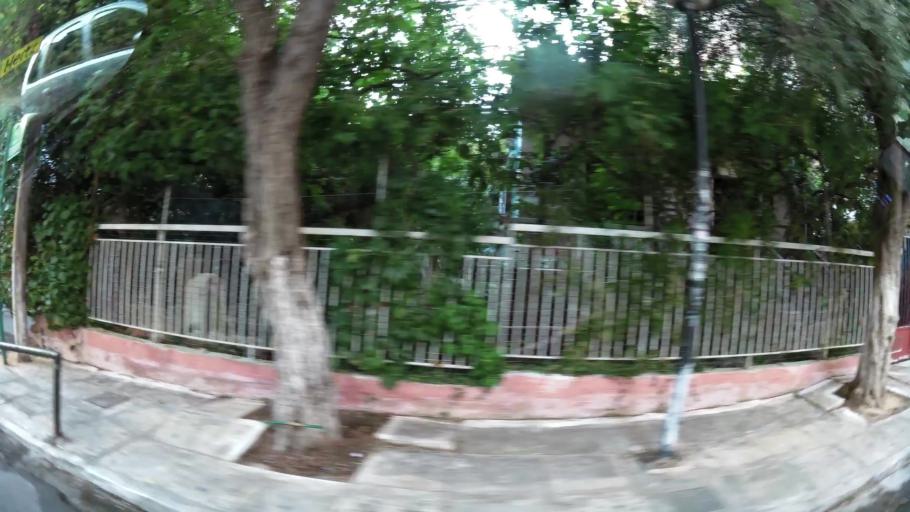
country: GR
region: Attica
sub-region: Nomarchia Athinas
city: Irakleio
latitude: 38.0457
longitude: 23.7754
